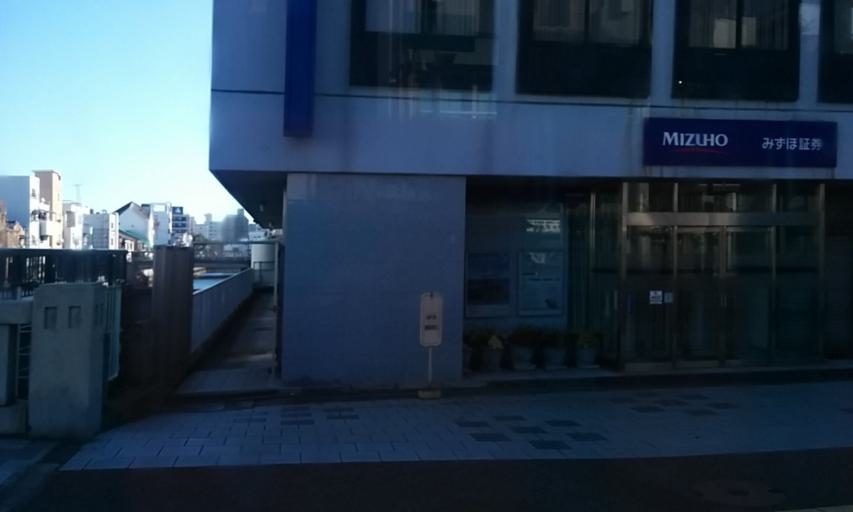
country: JP
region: Wakayama
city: Wakayama-shi
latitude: 34.2323
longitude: 135.1746
